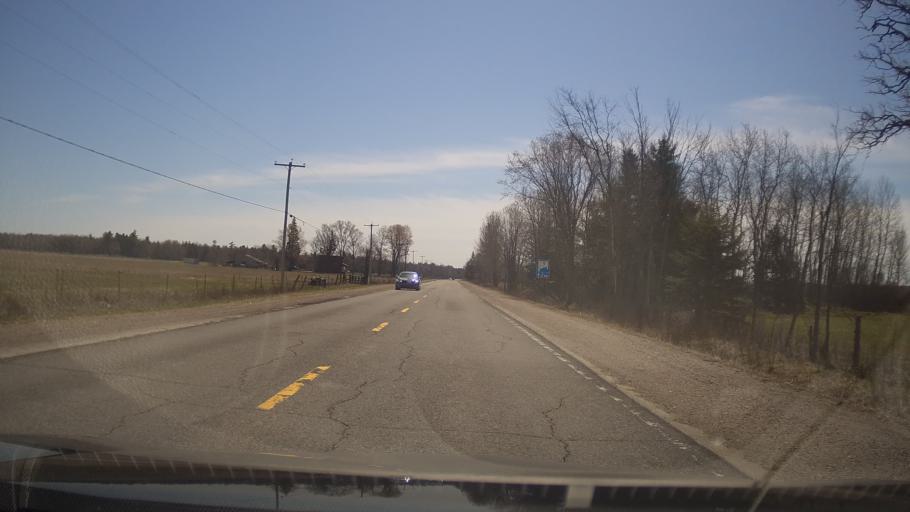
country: CA
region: Ontario
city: Arnprior
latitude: 45.5437
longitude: -76.3403
